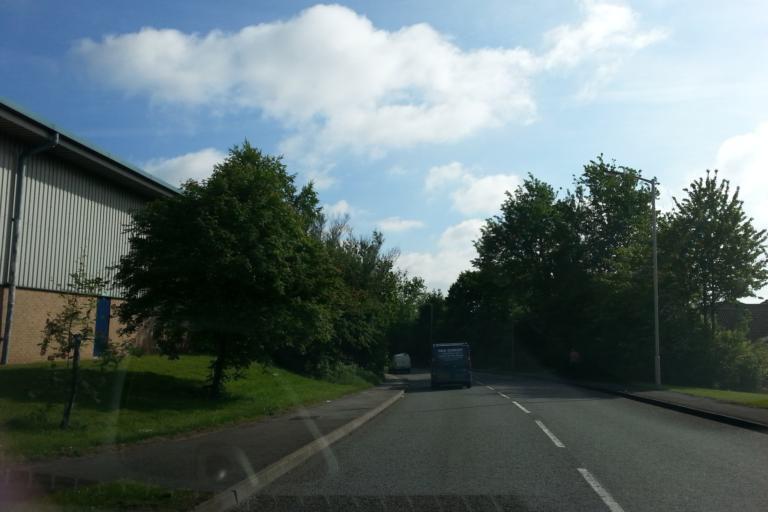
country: GB
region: England
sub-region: Nottinghamshire
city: Mansfield
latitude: 53.1311
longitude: -1.2182
